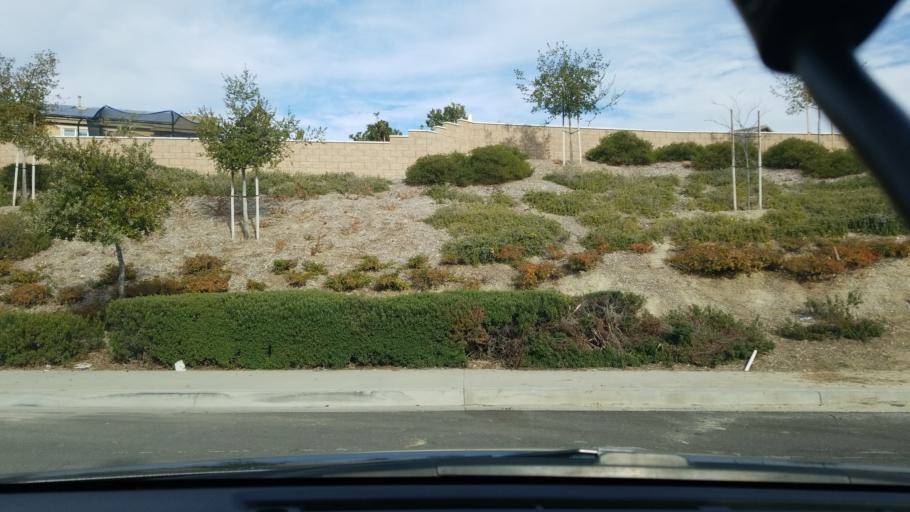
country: US
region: California
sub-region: Riverside County
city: Temecula
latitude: 33.4706
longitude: -117.0610
